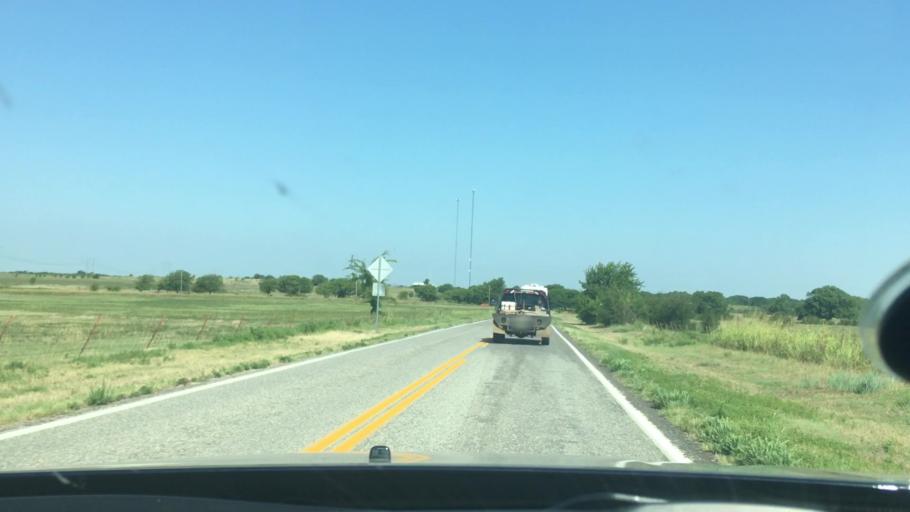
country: US
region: Oklahoma
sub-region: Johnston County
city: Tishomingo
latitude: 34.1877
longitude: -96.5276
